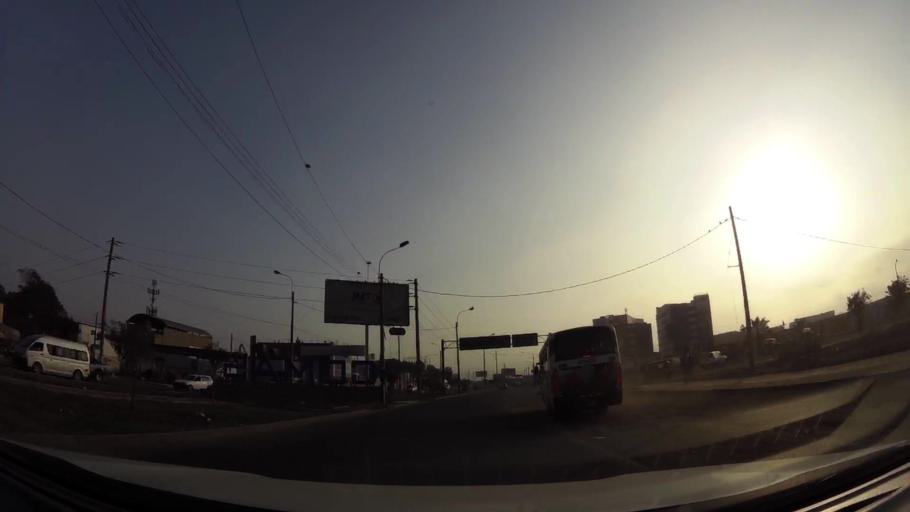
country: PE
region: Lima
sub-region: Lima
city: Independencia
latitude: -11.9616
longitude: -77.0631
